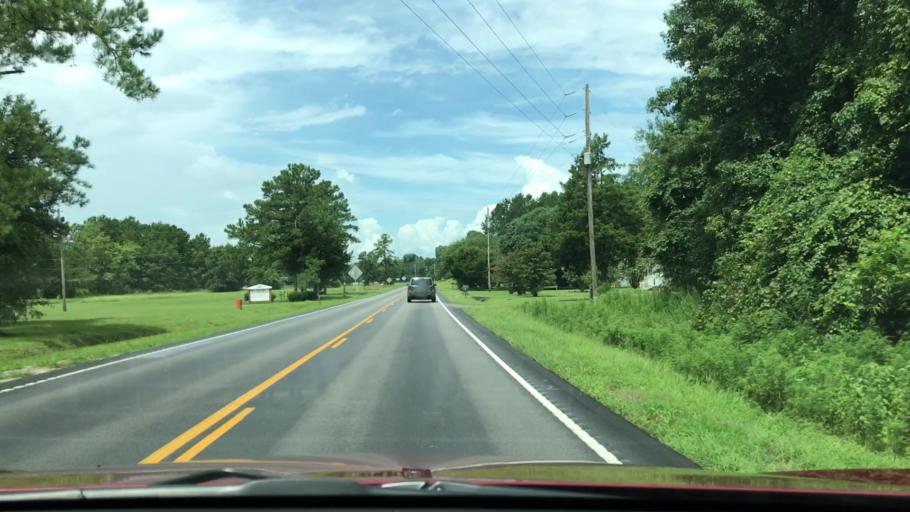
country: US
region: South Carolina
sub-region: Horry County
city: Loris
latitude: 33.9009
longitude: -78.8795
